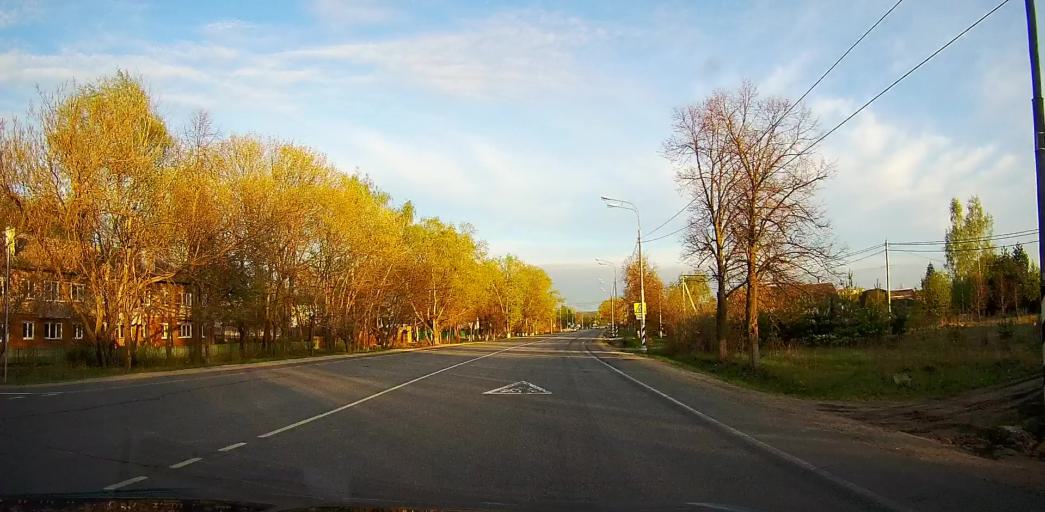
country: RU
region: Moskovskaya
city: Troitskoye
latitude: 55.2091
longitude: 38.6068
